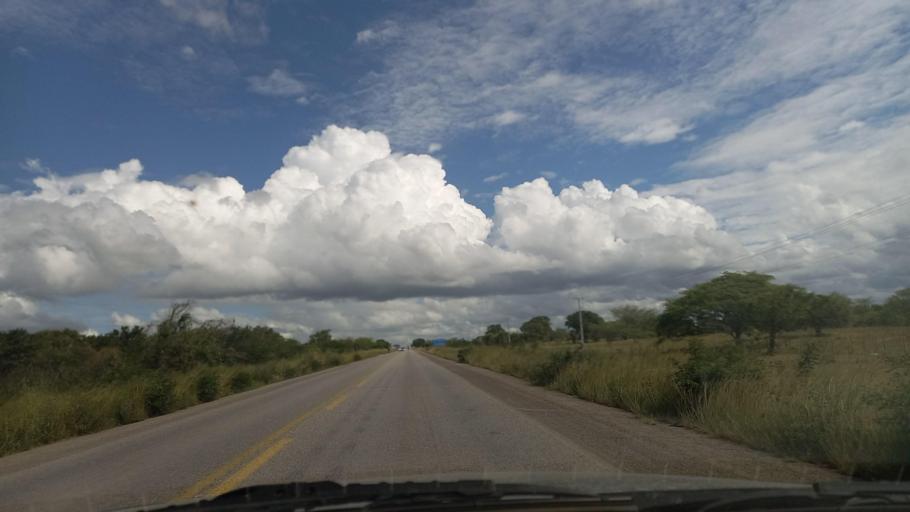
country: BR
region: Pernambuco
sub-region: Cachoeirinha
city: Cachoeirinha
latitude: -8.4581
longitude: -36.2144
